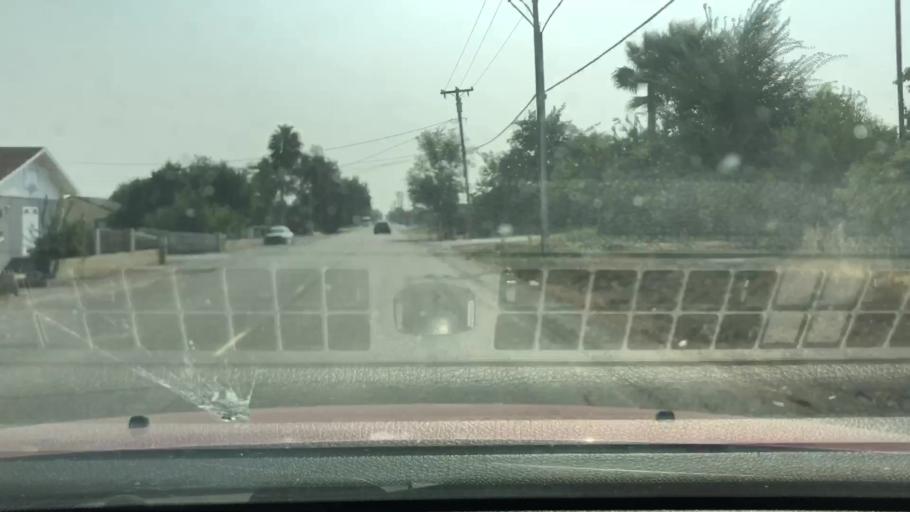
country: US
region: California
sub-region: San Joaquin County
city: Tracy
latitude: 37.7651
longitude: -121.4373
